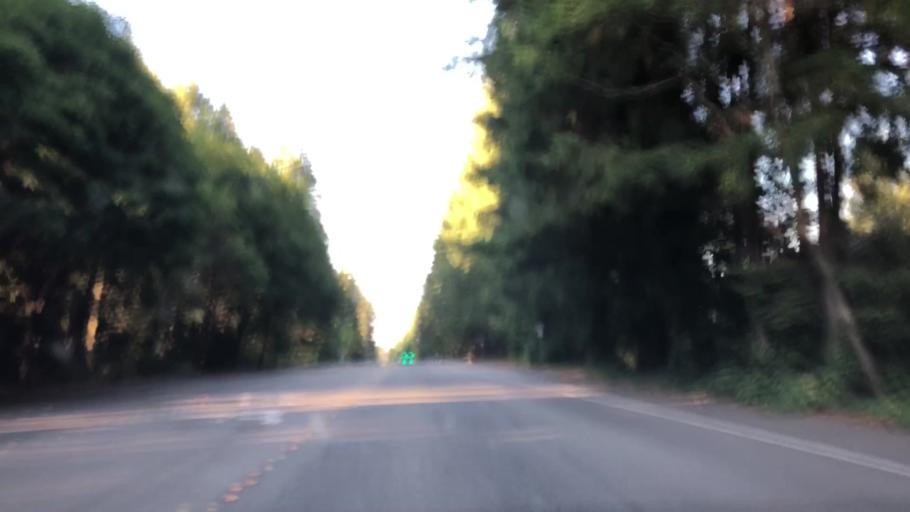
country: US
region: Washington
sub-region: King County
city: Redmond
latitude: 47.6352
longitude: -122.1279
